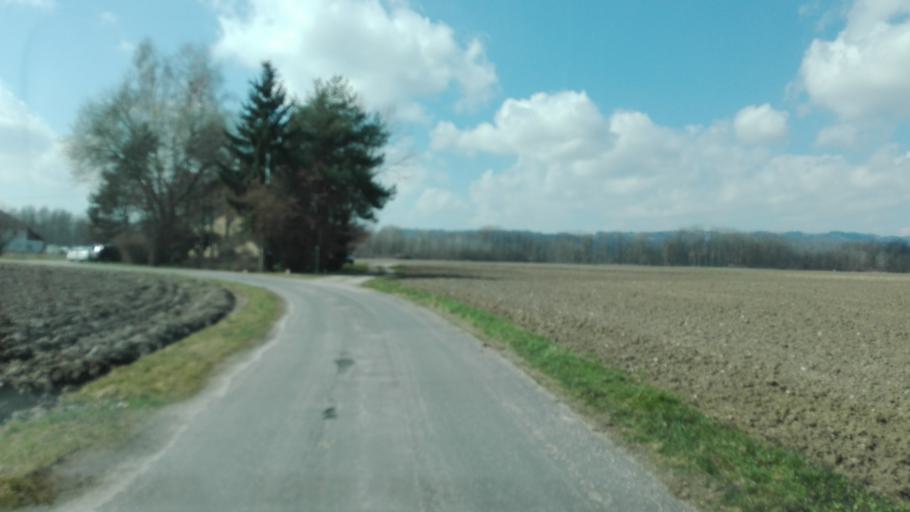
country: AT
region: Upper Austria
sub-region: Politischer Bezirk Urfahr-Umgebung
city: Feldkirchen an der Donau
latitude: 48.3389
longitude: 14.0415
